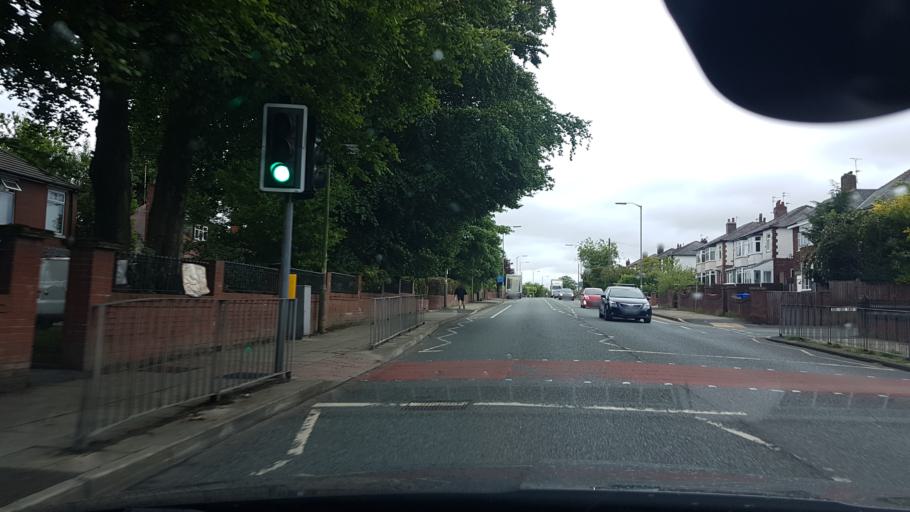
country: GB
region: England
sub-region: Borough of Bury
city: Radcliffe
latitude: 53.5865
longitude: -2.3242
